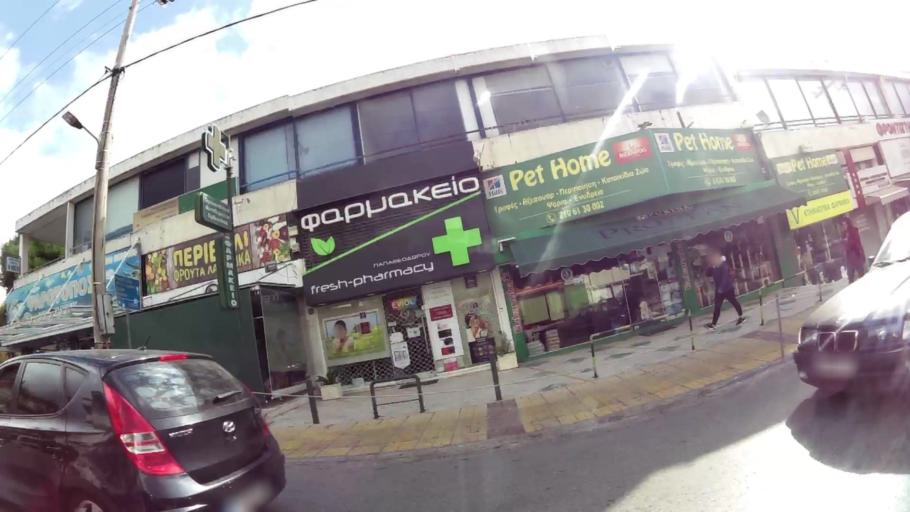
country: GR
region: Attica
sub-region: Nomarchia Athinas
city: Melissia
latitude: 38.0606
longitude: 23.8365
